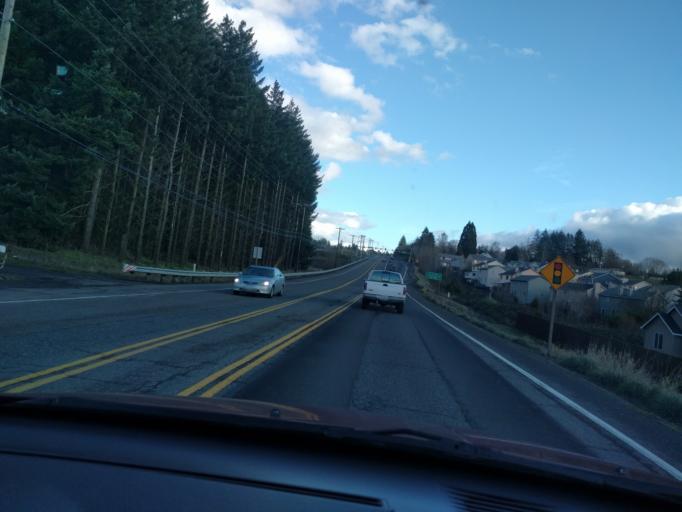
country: US
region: Oregon
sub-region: Clackamas County
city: Damascus
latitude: 45.4104
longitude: -122.4905
